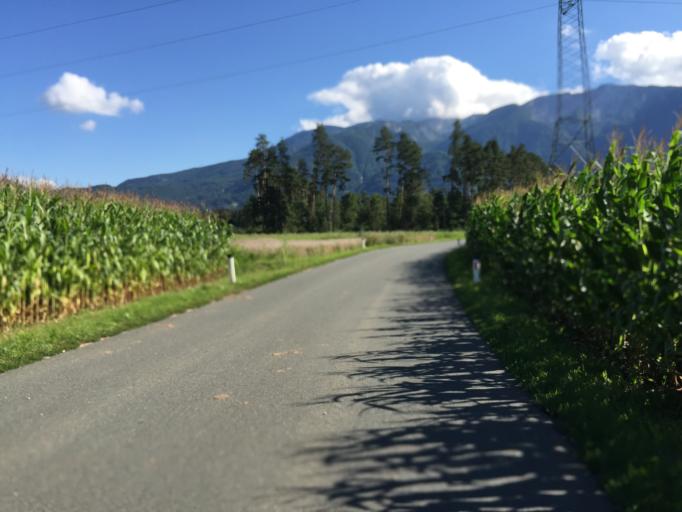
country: AT
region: Carinthia
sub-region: Politischer Bezirk Volkermarkt
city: Feistritz ob Bleiburg
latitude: 46.5686
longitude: 14.7704
